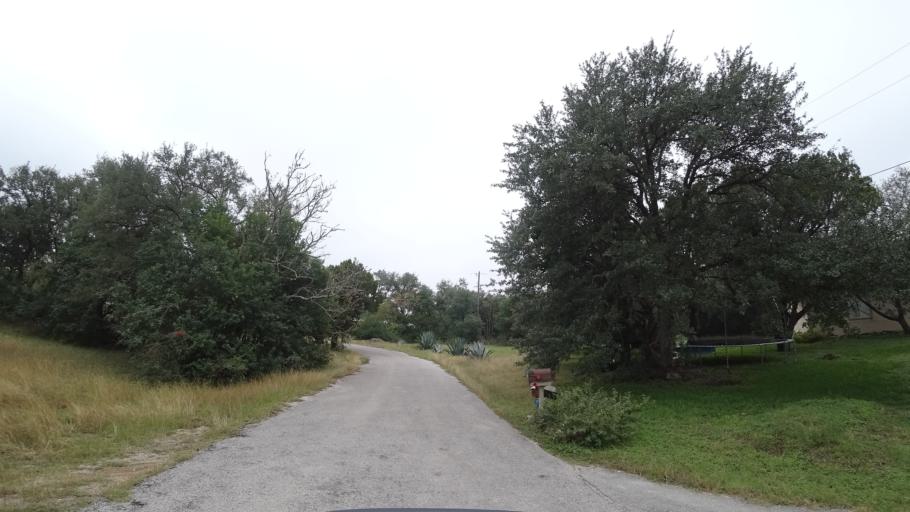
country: US
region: Texas
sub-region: Travis County
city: Barton Creek
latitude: 30.2328
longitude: -97.8960
